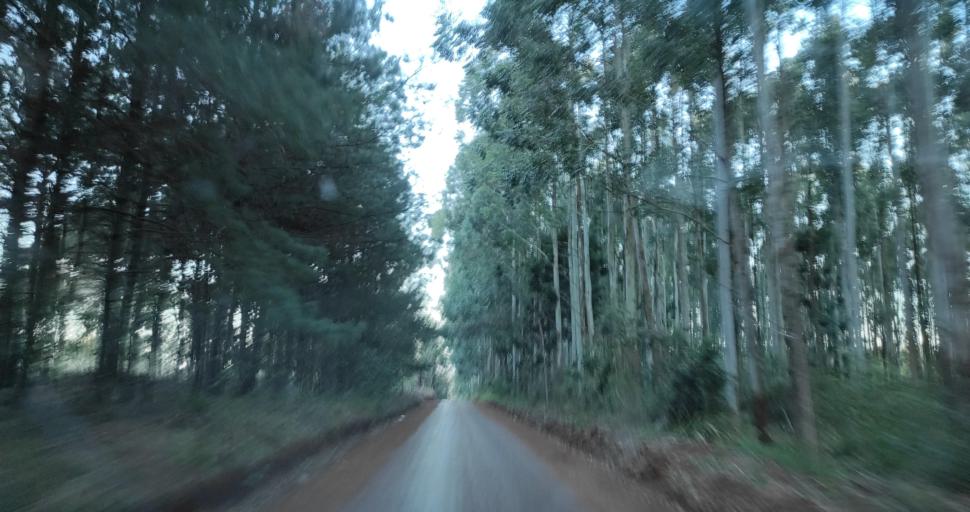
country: AR
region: Misiones
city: Capiovi
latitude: -26.8884
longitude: -55.0786
